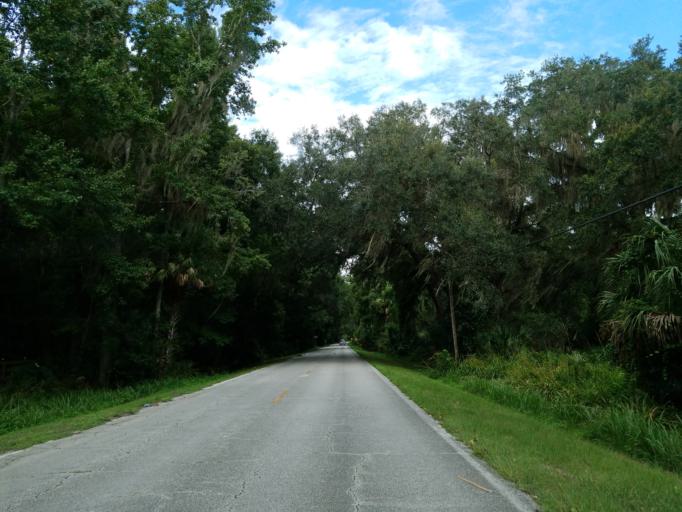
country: US
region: Florida
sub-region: Alachua County
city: Gainesville
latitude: 29.5023
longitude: -82.2693
